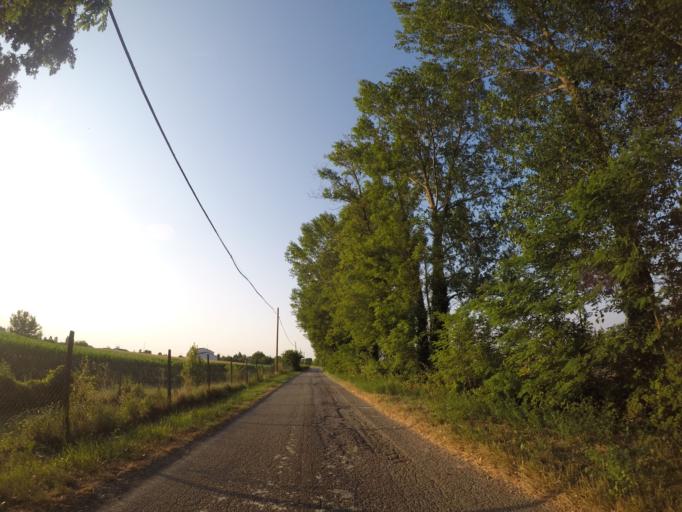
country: IT
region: Veneto
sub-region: Provincia di Rovigo
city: Fratta Polesine
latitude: 45.0072
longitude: 11.6418
